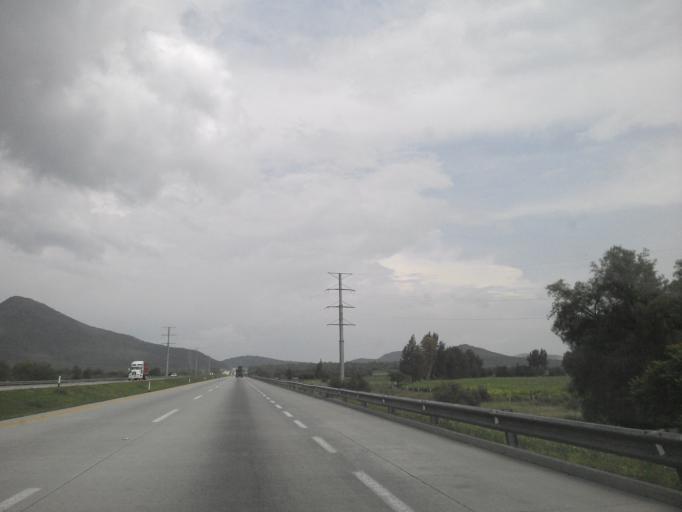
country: MX
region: Hidalgo
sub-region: Atitalaquia
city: Tezoquipa
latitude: 20.0456
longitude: -99.1851
